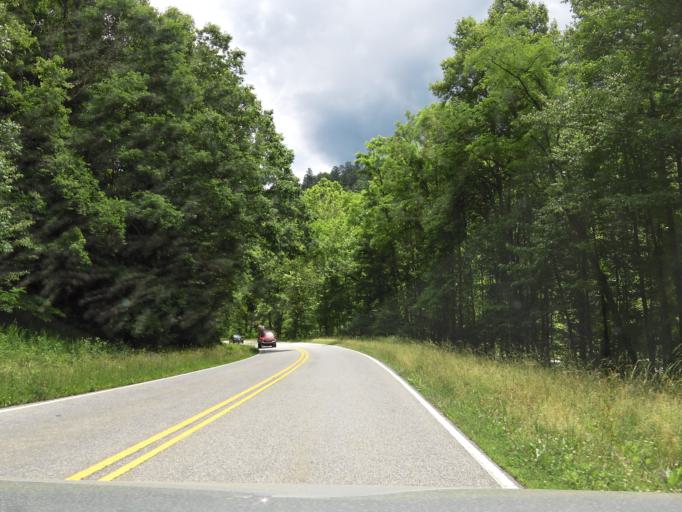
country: US
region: North Carolina
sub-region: Graham County
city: Robbinsville
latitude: 35.4232
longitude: -83.9028
